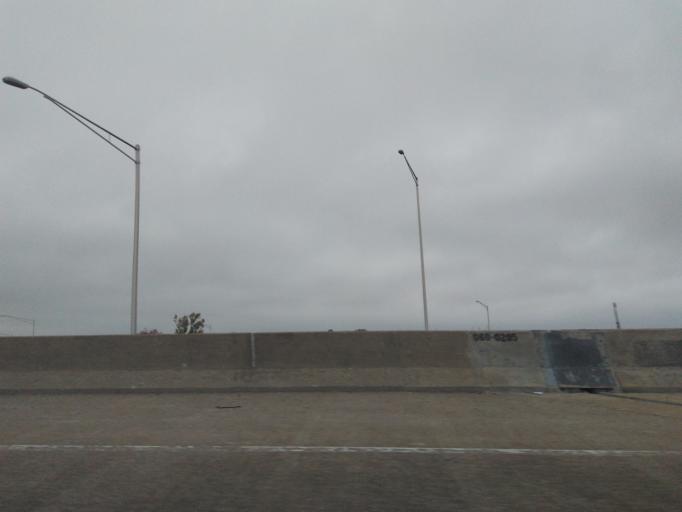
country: US
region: Illinois
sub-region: Saint Clair County
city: Caseyville
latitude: 38.6721
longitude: -90.0330
